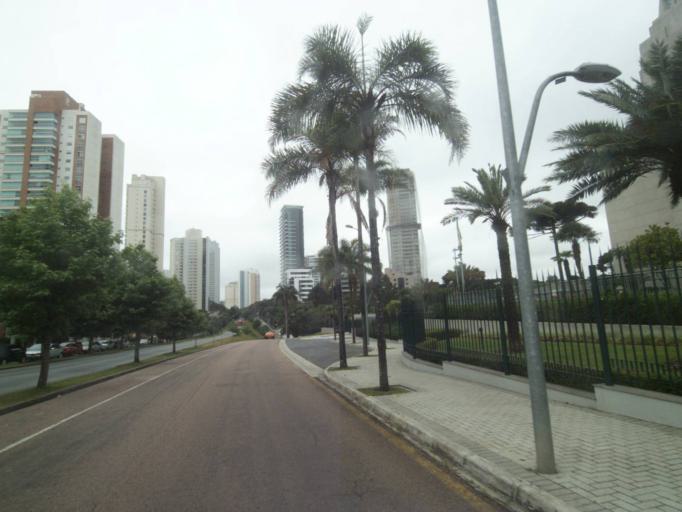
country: BR
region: Parana
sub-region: Curitiba
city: Curitiba
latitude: -25.4411
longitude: -49.3422
